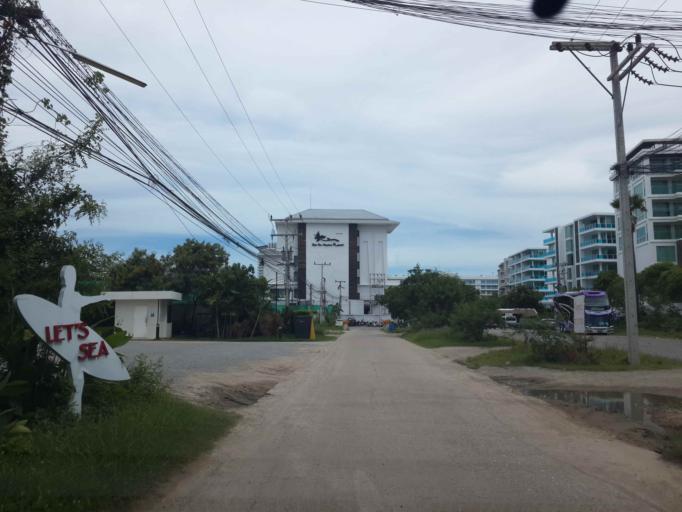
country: TH
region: Prachuap Khiri Khan
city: Hua Hin
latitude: 12.5322
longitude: 99.9685
